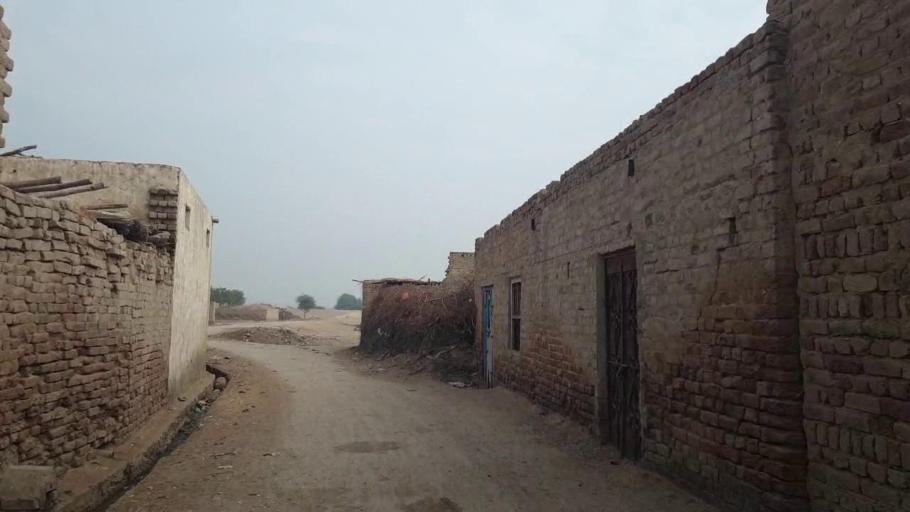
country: PK
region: Sindh
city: Sann
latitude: 25.9774
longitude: 68.1920
